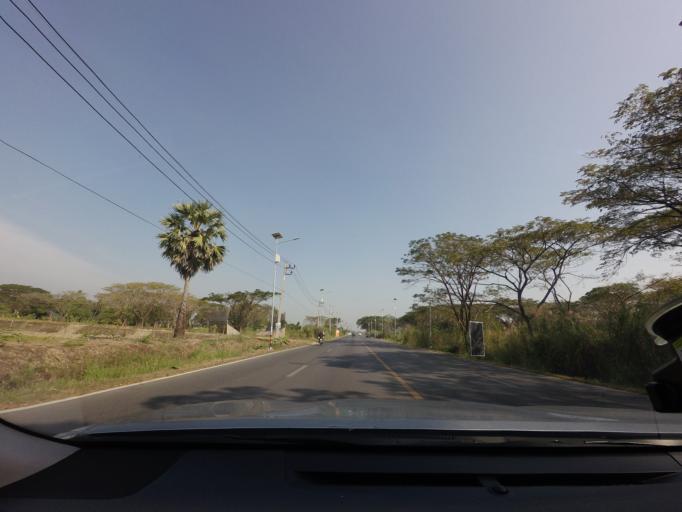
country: TH
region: Nakhon Si Thammarat
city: Nakhon Si Thammarat
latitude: 8.4480
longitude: 99.9815
